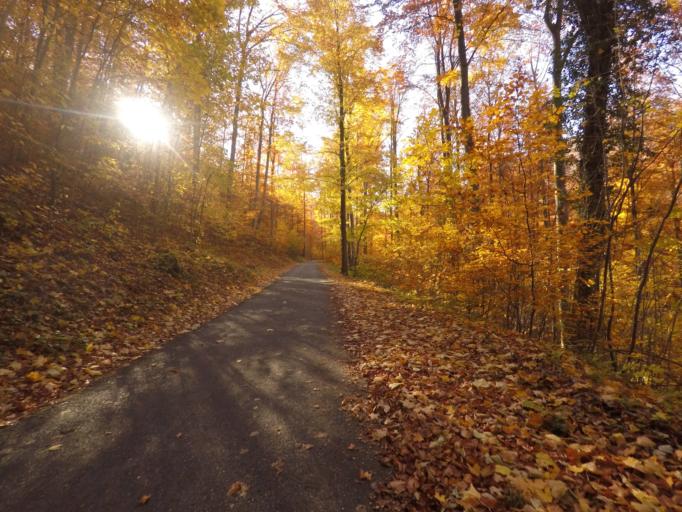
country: DE
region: Baden-Wuerttemberg
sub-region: Tuebingen Region
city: Pfullingen
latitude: 48.4398
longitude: 9.2373
